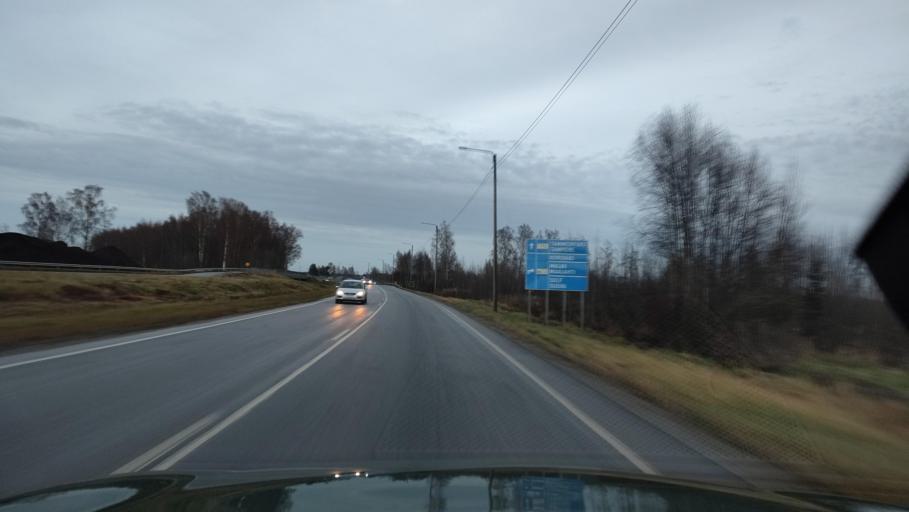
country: FI
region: Ostrobothnia
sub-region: Vaasa
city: Ristinummi
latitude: 63.0416
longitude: 21.7391
